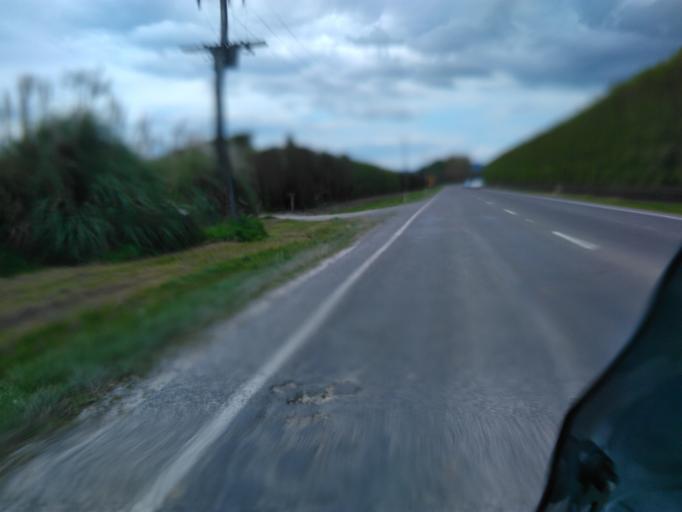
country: NZ
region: Gisborne
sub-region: Gisborne District
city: Gisborne
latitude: -38.6559
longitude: 177.9304
